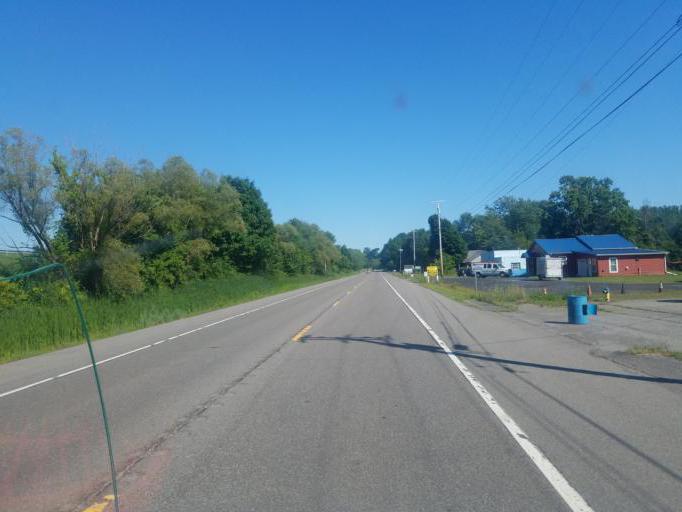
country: US
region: New York
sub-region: Wayne County
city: Lyons
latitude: 43.0630
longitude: -77.0221
